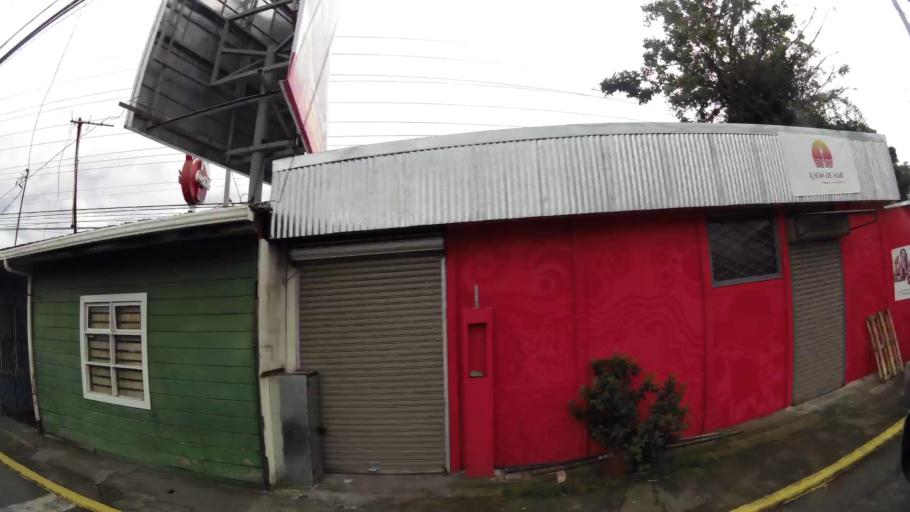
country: CR
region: San Jose
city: Calle Blancos
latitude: 9.9450
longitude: -84.0648
